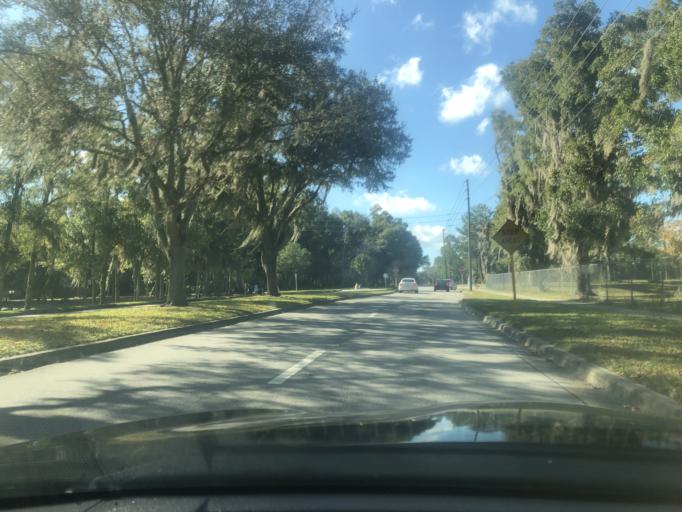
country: US
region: Florida
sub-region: Citrus County
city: Inverness
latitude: 28.8324
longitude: -82.3437
